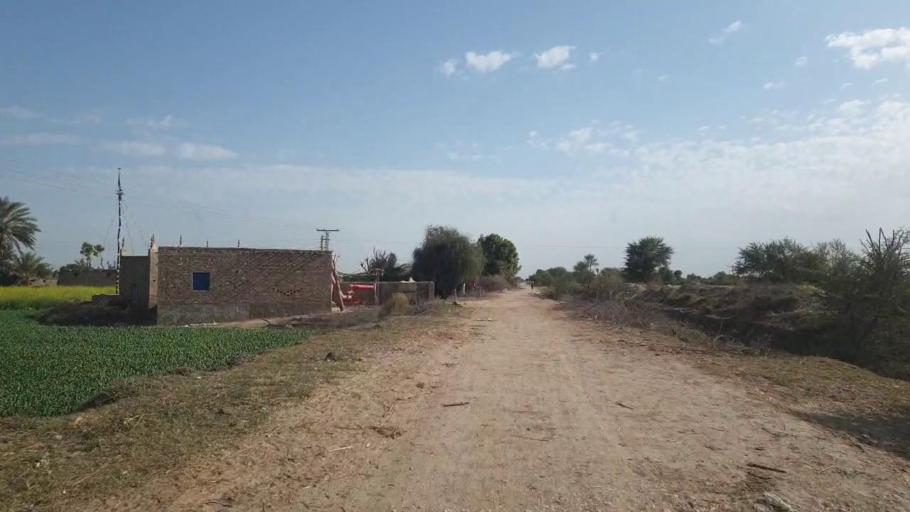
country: PK
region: Sindh
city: Shahdadpur
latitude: 26.0193
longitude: 68.4949
